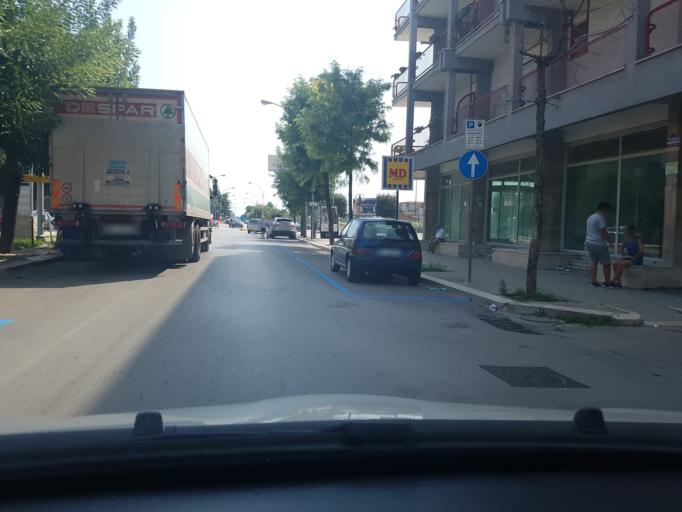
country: IT
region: Apulia
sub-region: Provincia di Foggia
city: Cerignola
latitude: 41.2631
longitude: 15.9118
